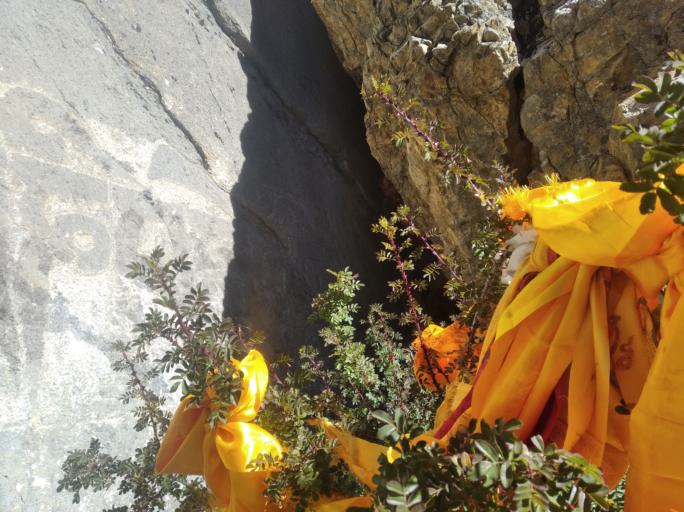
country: NP
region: Western Region
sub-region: Dhawalagiri Zone
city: Jomsom
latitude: 29.0717
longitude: 83.3428
